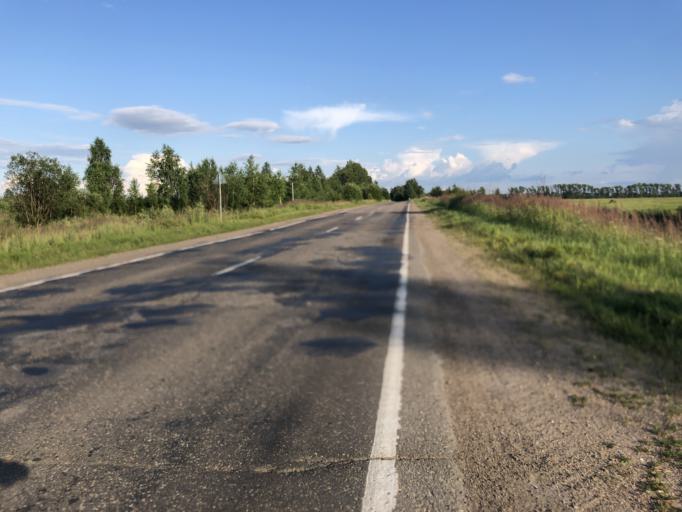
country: RU
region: Tverskaya
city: Rzhev
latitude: 56.2779
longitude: 34.2365
